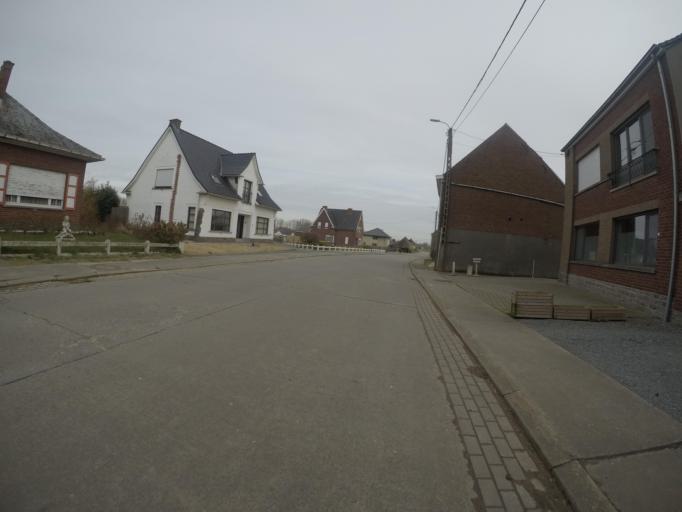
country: BE
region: Flanders
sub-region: Provincie Oost-Vlaanderen
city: Sint-Maria-Lierde
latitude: 50.8014
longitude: 3.8459
